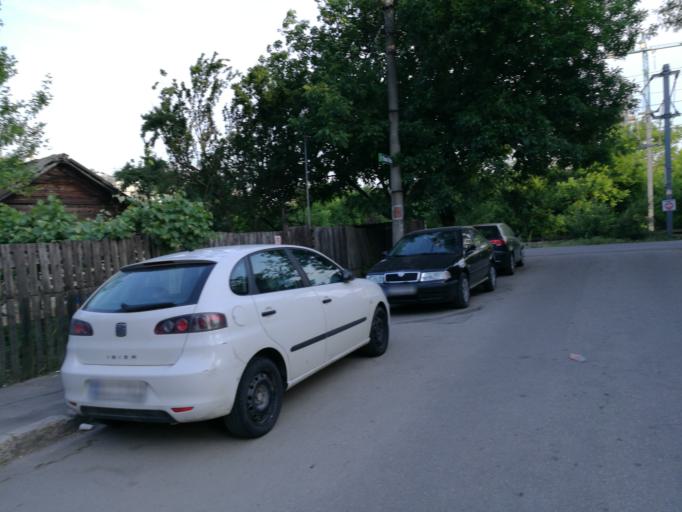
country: RO
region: Bucuresti
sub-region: Municipiul Bucuresti
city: Bucharest
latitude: 44.4898
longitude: 26.0932
